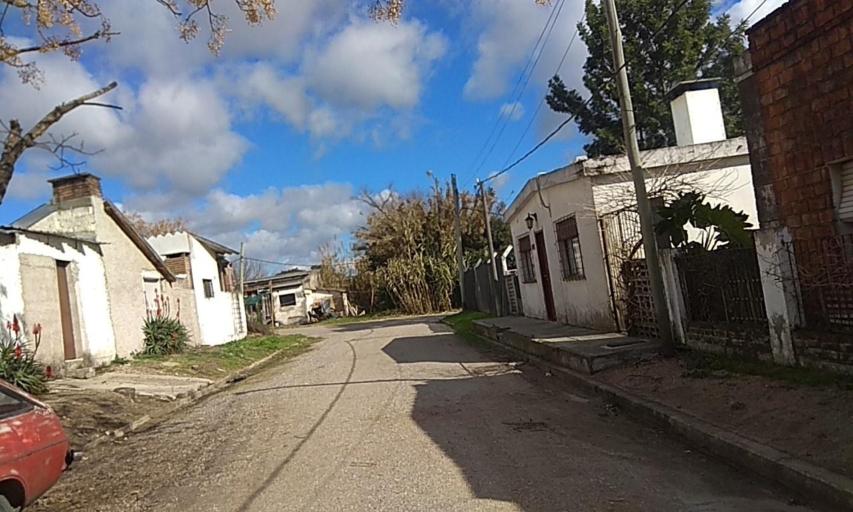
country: UY
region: Florida
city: Florida
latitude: -34.0911
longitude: -56.2221
